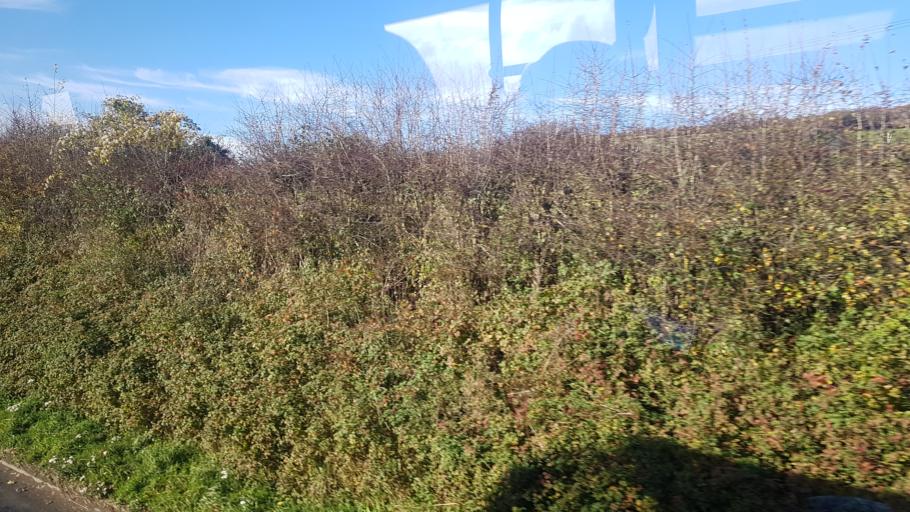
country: GB
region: England
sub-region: Isle of Wight
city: Newport
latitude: 50.6854
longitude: -1.3246
